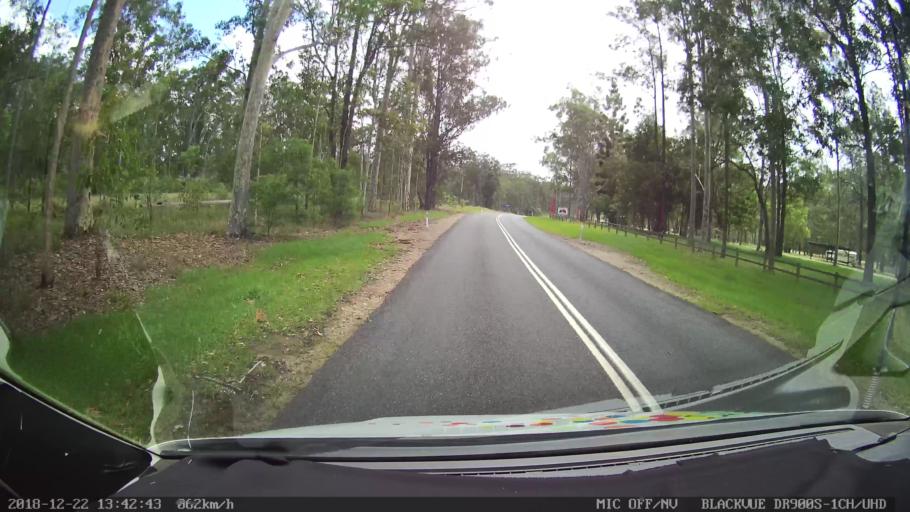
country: AU
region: New South Wales
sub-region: Clarence Valley
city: Coutts Crossing
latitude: -29.9251
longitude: 152.7505
